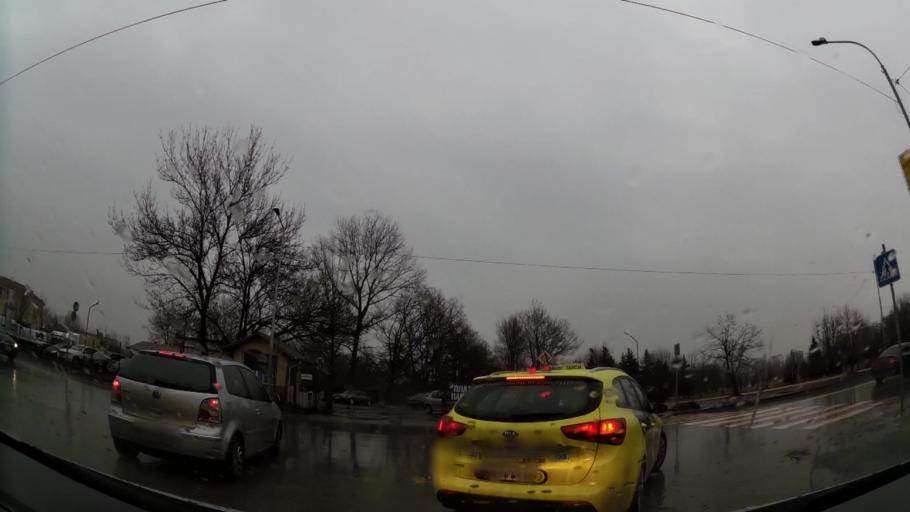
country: BG
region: Sofia-Capital
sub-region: Stolichna Obshtina
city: Sofia
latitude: 42.6535
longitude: 23.3473
